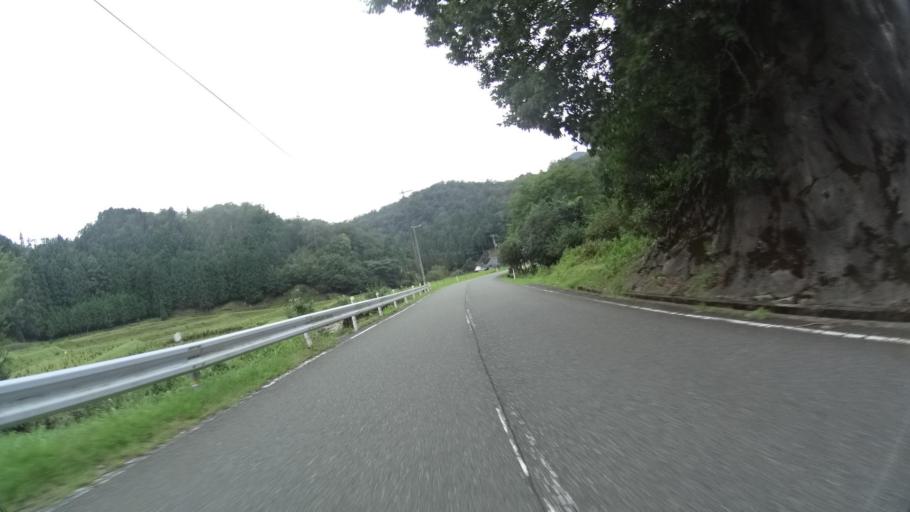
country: JP
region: Kyoto
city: Miyazu
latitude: 35.4635
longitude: 135.1533
